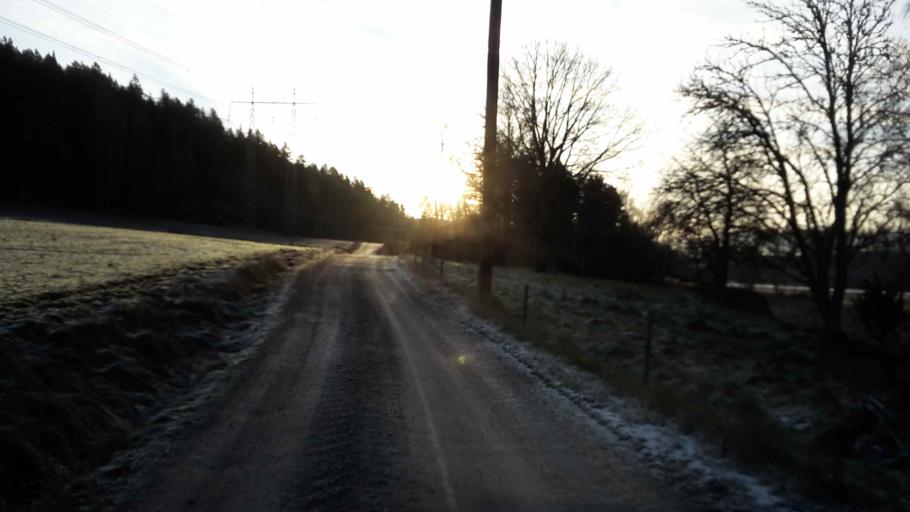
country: SE
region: OEstergoetland
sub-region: Atvidabergs Kommun
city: Atvidaberg
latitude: 58.2690
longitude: 16.1309
